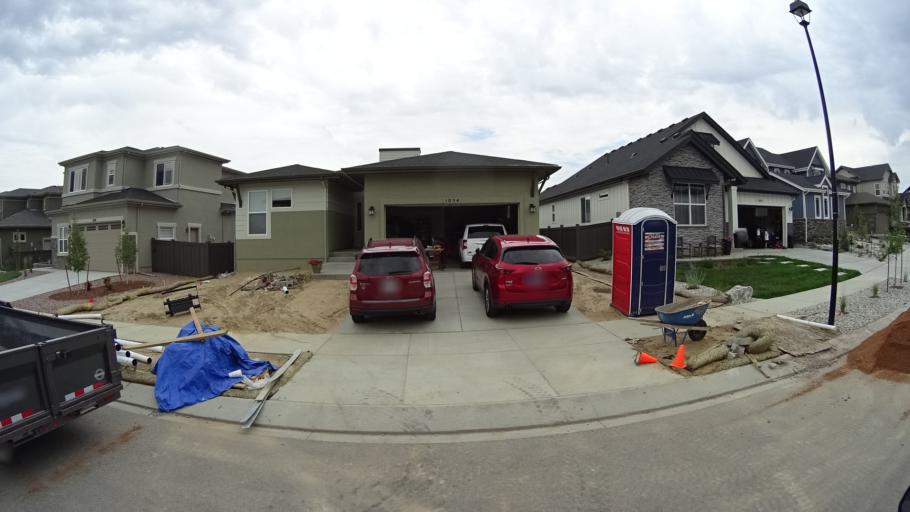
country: US
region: Colorado
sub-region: El Paso County
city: Gleneagle
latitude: 39.0042
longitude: -104.8110
